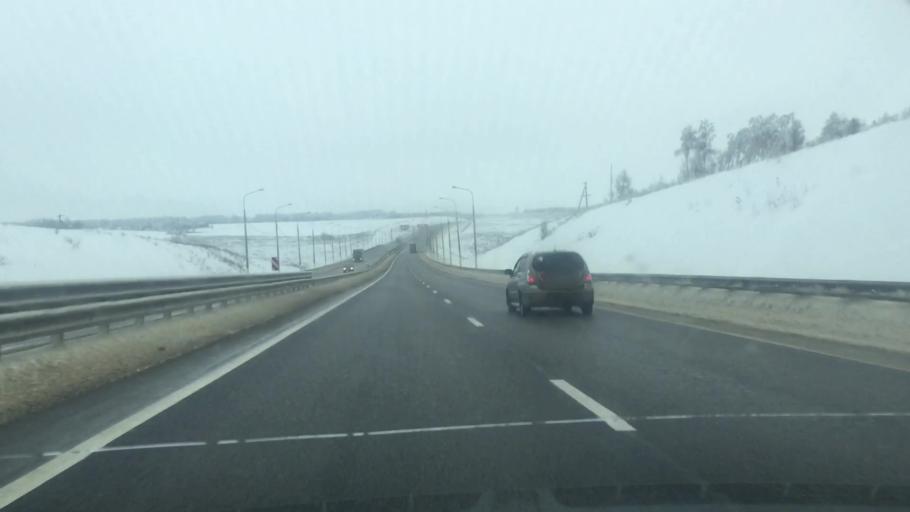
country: RU
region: Lipetsk
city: Stanovoye
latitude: 52.8684
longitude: 38.2830
